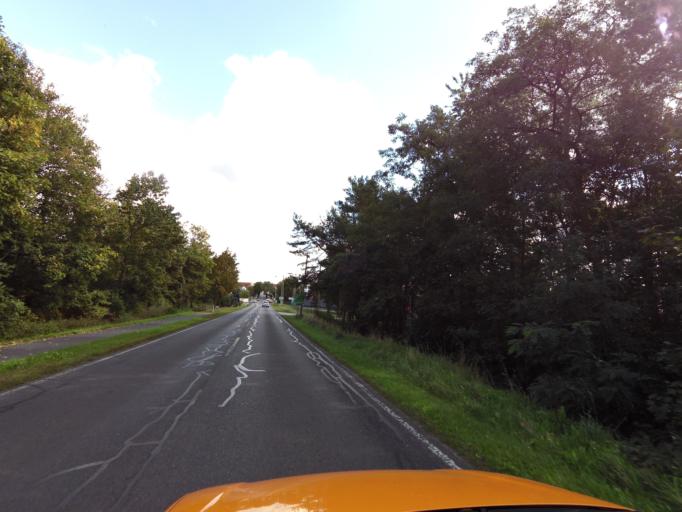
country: DE
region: Brandenburg
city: Luckenwalde
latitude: 52.0961
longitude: 13.1498
